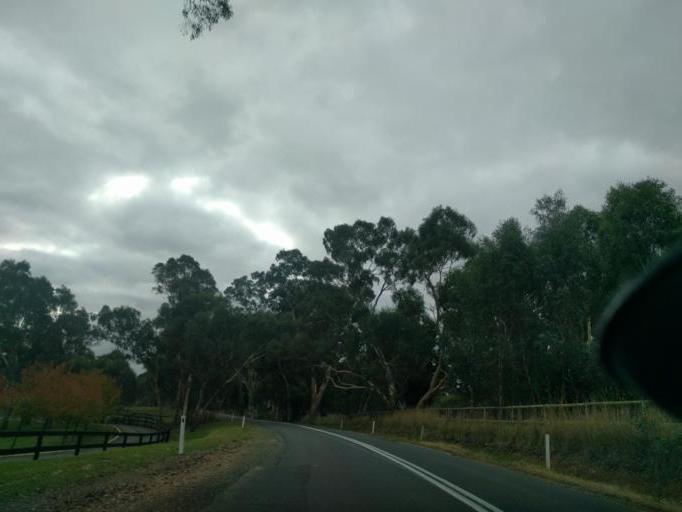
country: AU
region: South Australia
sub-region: Mount Barker
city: Hahndorf
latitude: -35.0759
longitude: 138.7795
